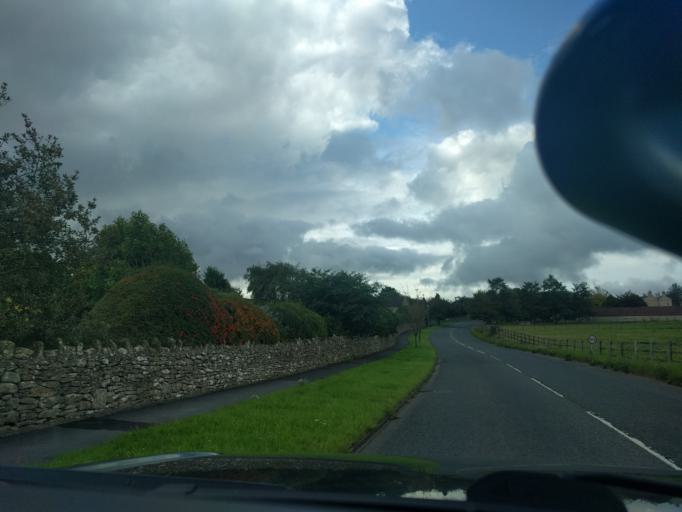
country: GB
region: England
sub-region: Bath and North East Somerset
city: Freshford
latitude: 51.3501
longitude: -2.2900
